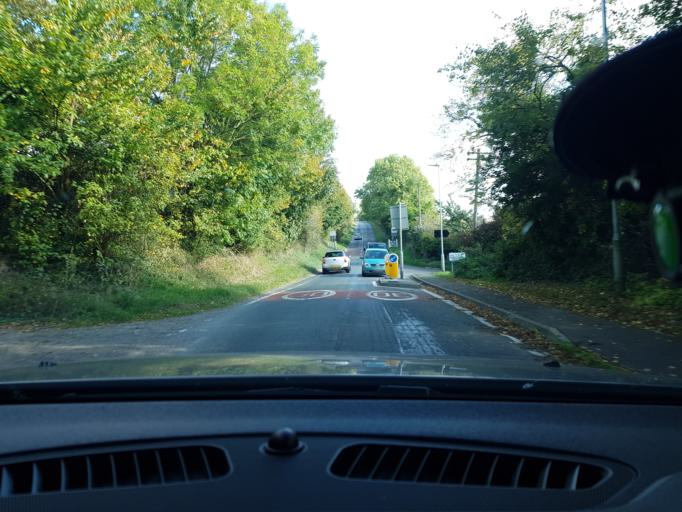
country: GB
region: England
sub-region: Wiltshire
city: Aldbourne
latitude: 51.4986
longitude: -1.5915
